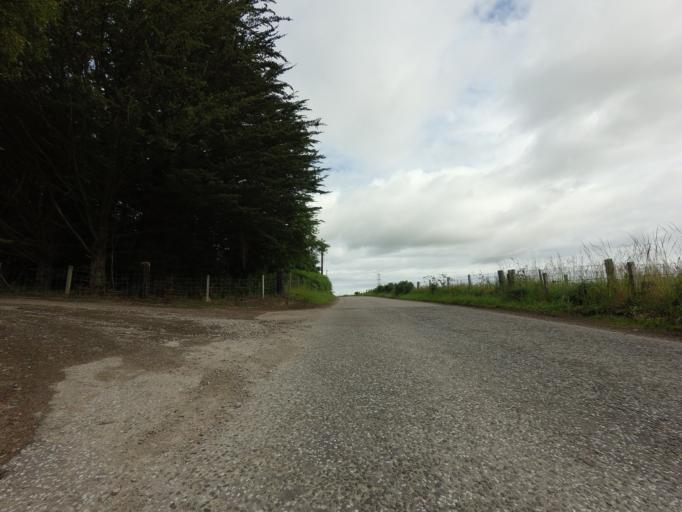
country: GB
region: Scotland
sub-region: Moray
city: Elgin
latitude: 57.6595
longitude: -3.3546
